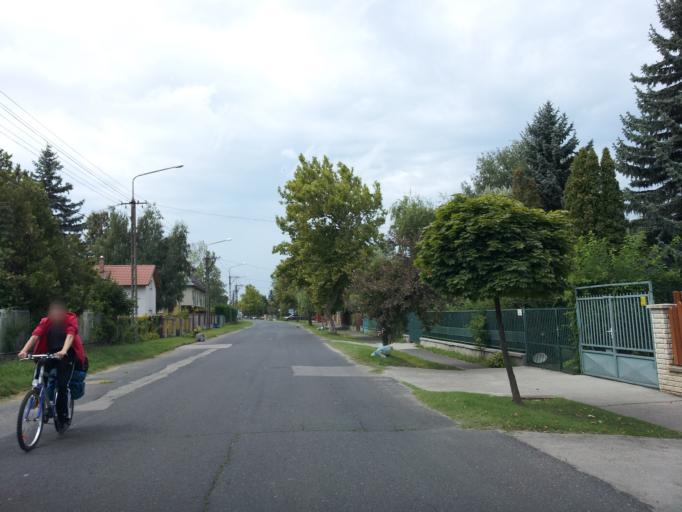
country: HU
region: Somogy
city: Zamardi
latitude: 46.8899
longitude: 17.9748
